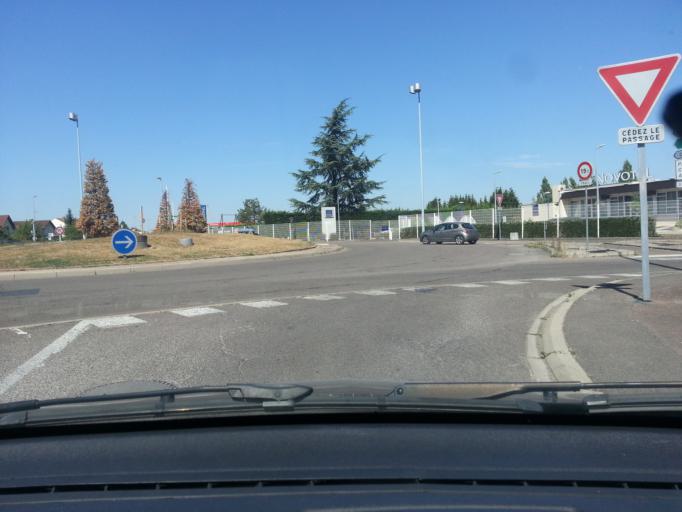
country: FR
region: Bourgogne
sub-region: Departement de la Cote-d'Or
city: Perrigny-les-Dijon
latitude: 47.2791
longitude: 5.0072
